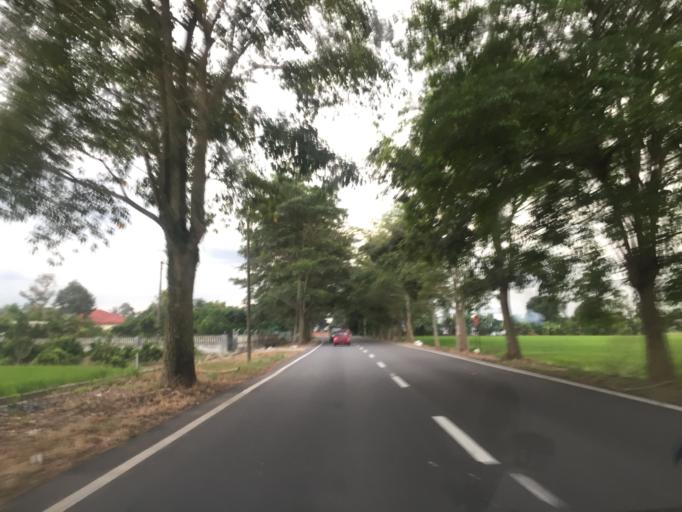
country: MY
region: Penang
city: Tasek Glugor
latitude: 5.5401
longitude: 100.5086
